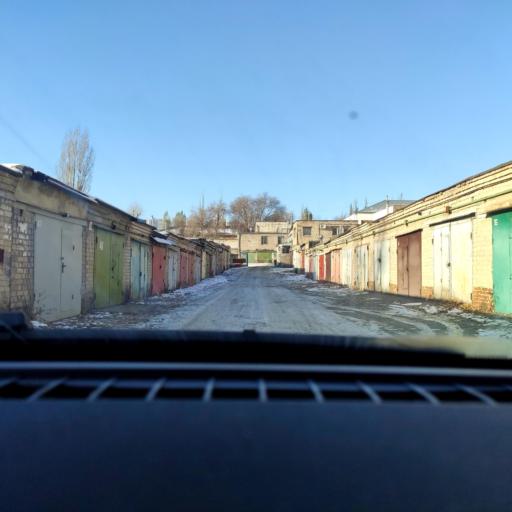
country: RU
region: Voronezj
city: Somovo
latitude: 51.7161
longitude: 39.2780
